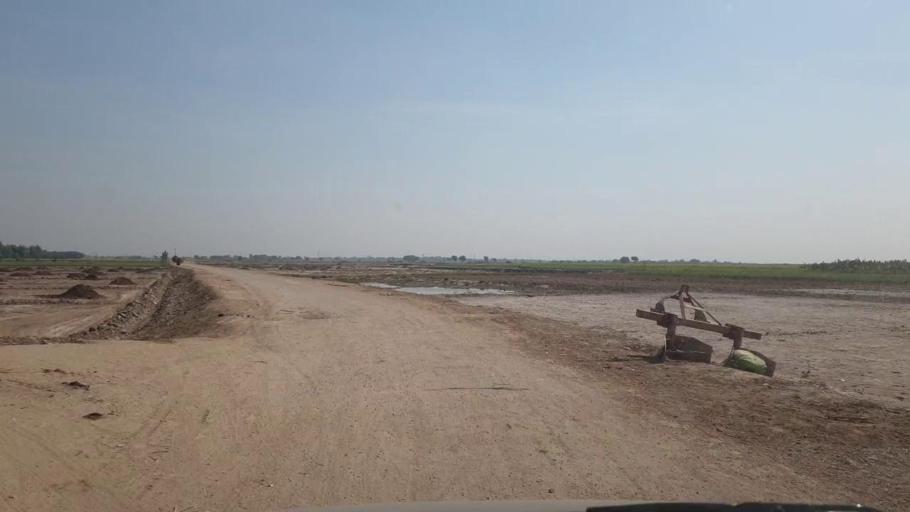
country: PK
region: Sindh
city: Chambar
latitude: 25.3738
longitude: 68.8089
